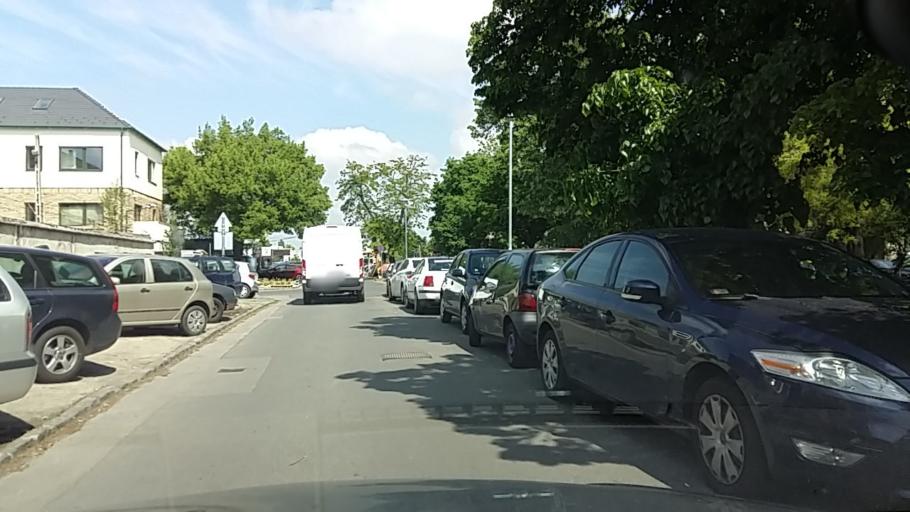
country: HU
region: Budapest
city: Budapest XIV. keruelet
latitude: 47.5022
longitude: 19.1184
